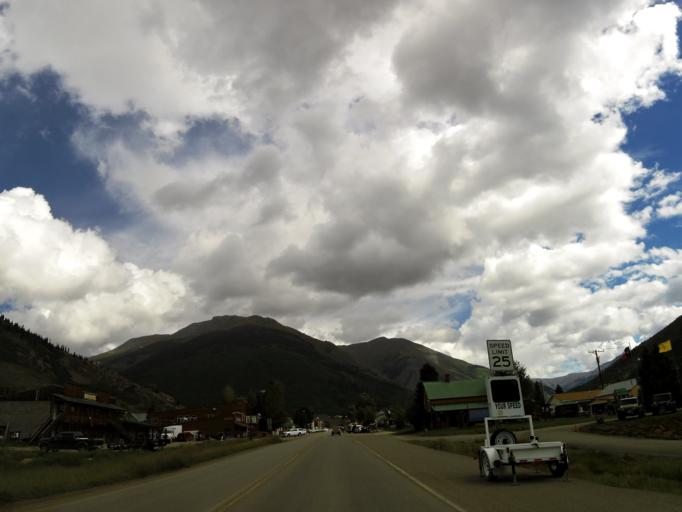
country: US
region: Colorado
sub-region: San Juan County
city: Silverton
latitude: 37.8067
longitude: -107.6689
